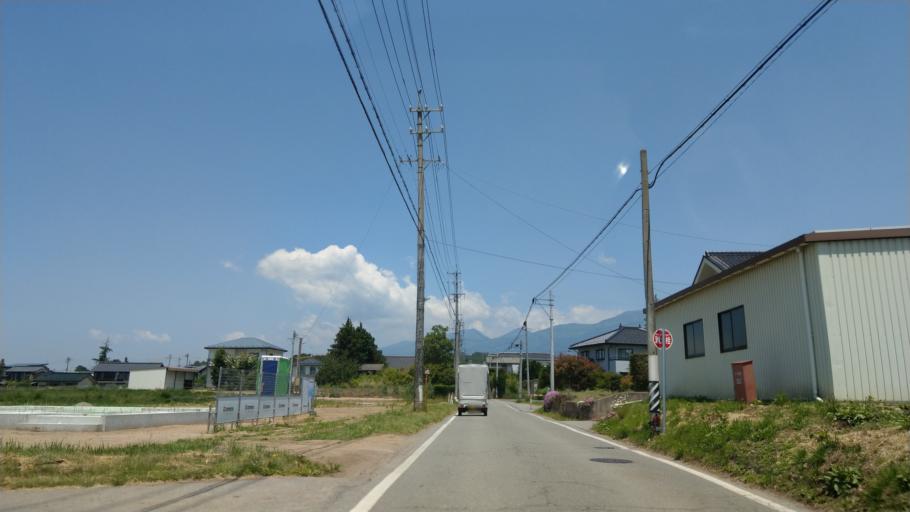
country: JP
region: Nagano
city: Komoro
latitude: 36.2962
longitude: 138.4395
